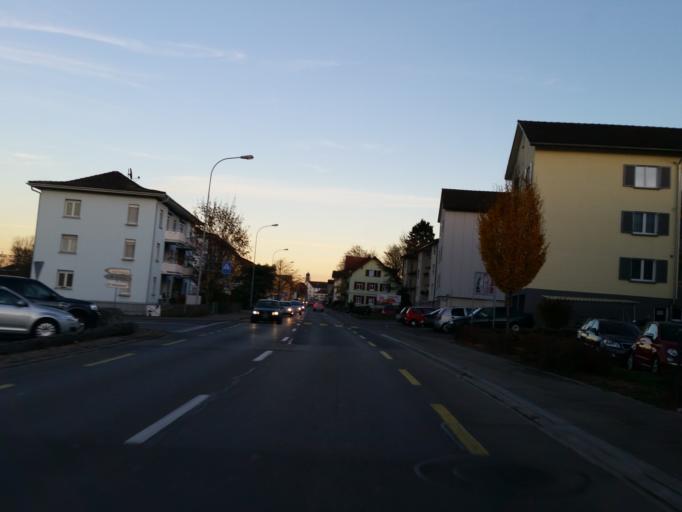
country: CH
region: Thurgau
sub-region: Kreuzlingen District
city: Munsterlingen
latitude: 47.6335
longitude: 9.2242
